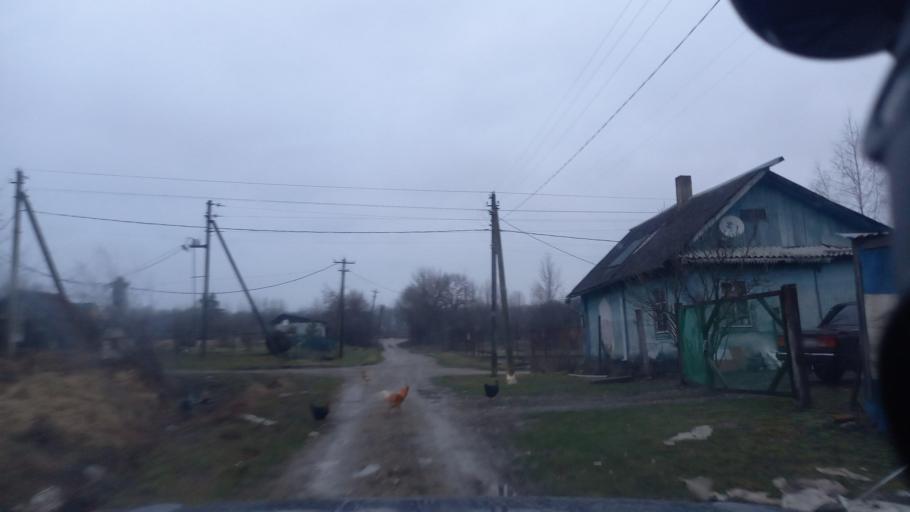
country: RU
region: Krasnodarskiy
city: Saratovskaya
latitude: 44.6459
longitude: 39.3093
